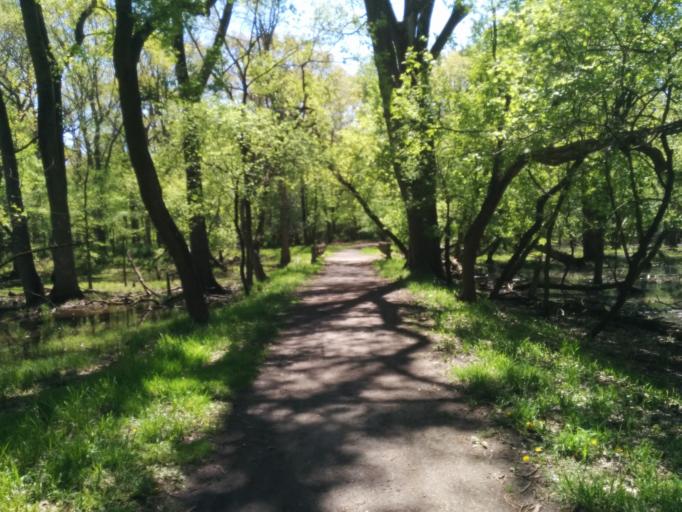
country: US
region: Illinois
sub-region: Cook County
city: Schiller Park
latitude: 41.9756
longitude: -87.8566
